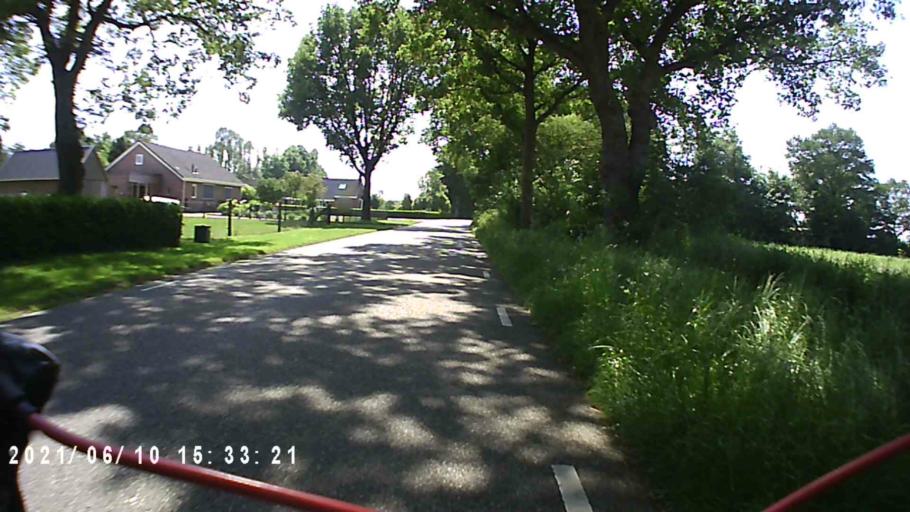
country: NL
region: Friesland
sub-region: Gemeente Achtkarspelen
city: Surhuisterveen
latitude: 53.1688
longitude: 6.1727
